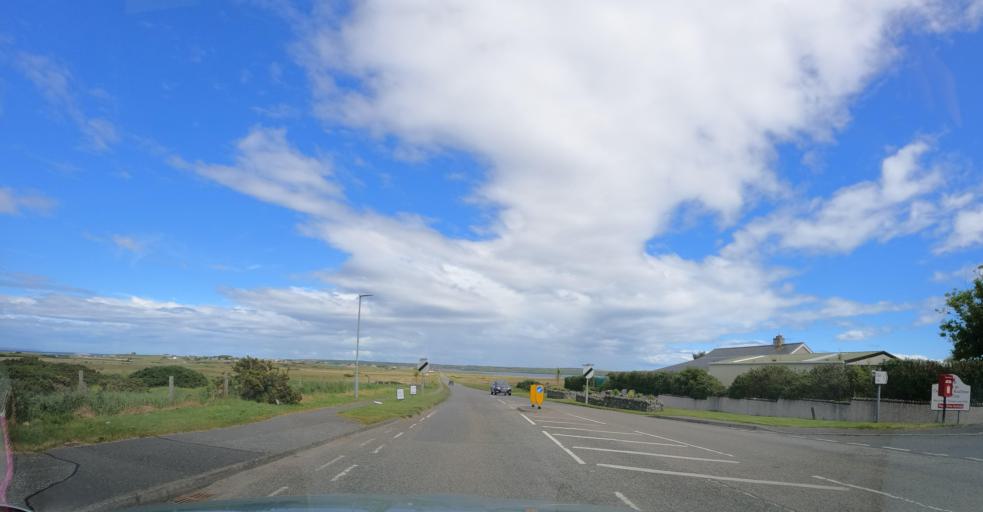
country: GB
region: Scotland
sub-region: Eilean Siar
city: Stornoway
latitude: 58.2028
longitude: -6.3381
